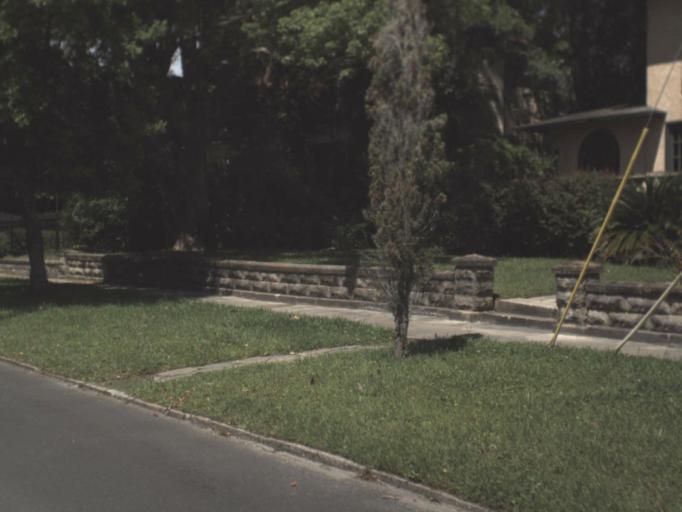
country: US
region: Florida
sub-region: Duval County
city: Jacksonville
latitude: 30.3051
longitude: -81.6942
